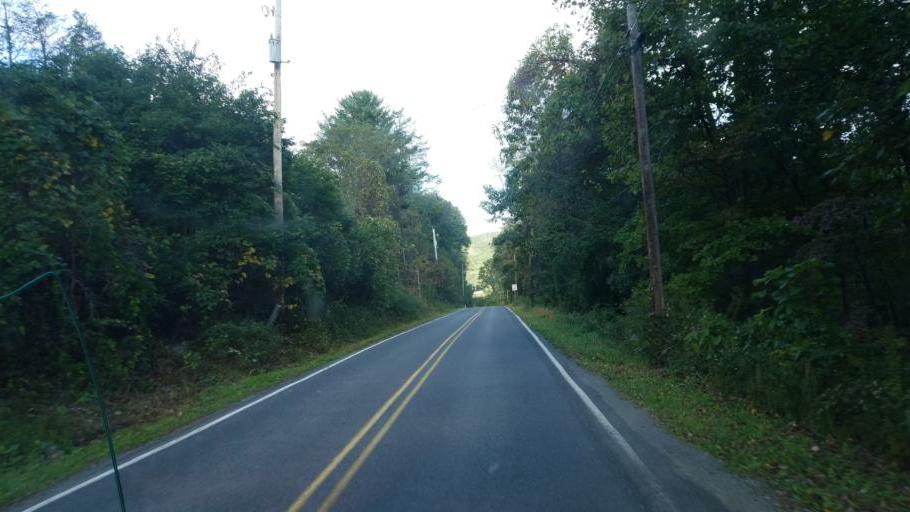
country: US
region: Pennsylvania
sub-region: Adams County
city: Biglerville
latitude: 39.8915
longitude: -77.3745
